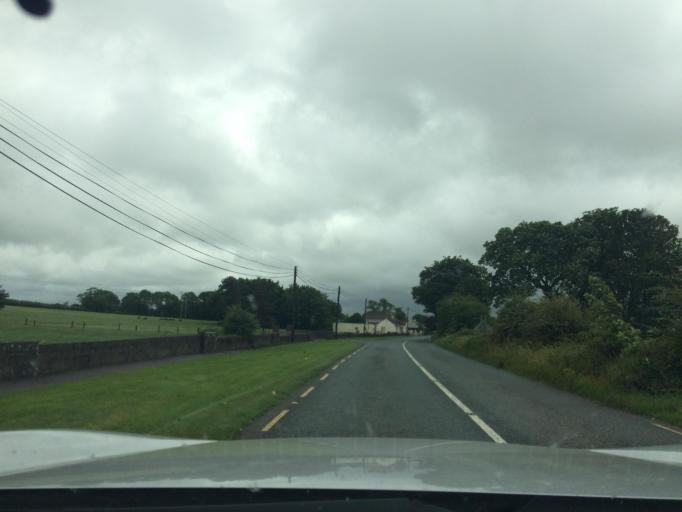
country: IE
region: Munster
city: Cashel
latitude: 52.5061
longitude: -7.8721
